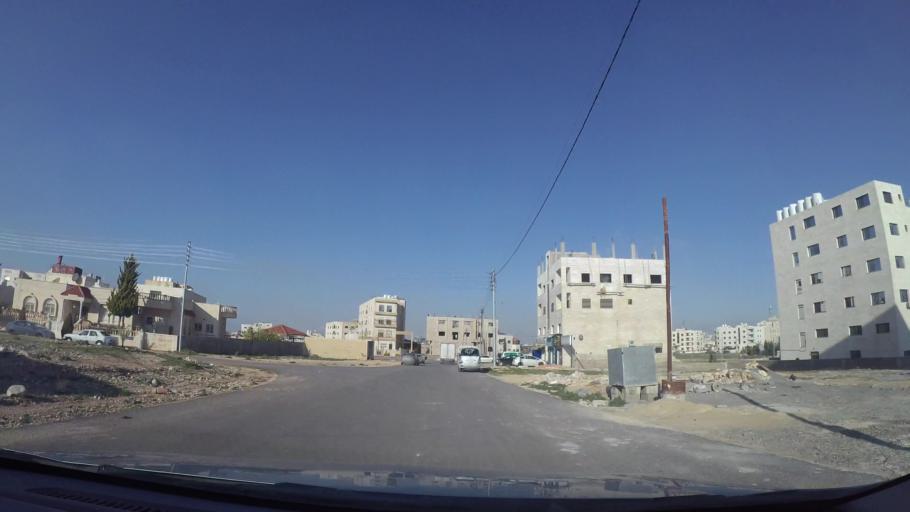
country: JO
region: Amman
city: Al Bunayyat ash Shamaliyah
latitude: 31.9010
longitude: 35.9228
